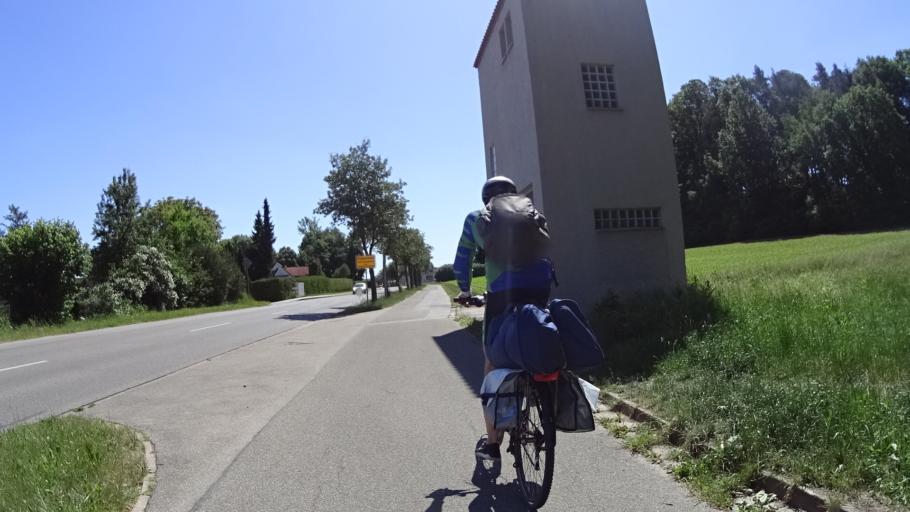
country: DE
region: Bavaria
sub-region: Regierungsbezirk Mittelfranken
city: Gunzenhausen
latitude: 49.1201
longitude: 10.7910
